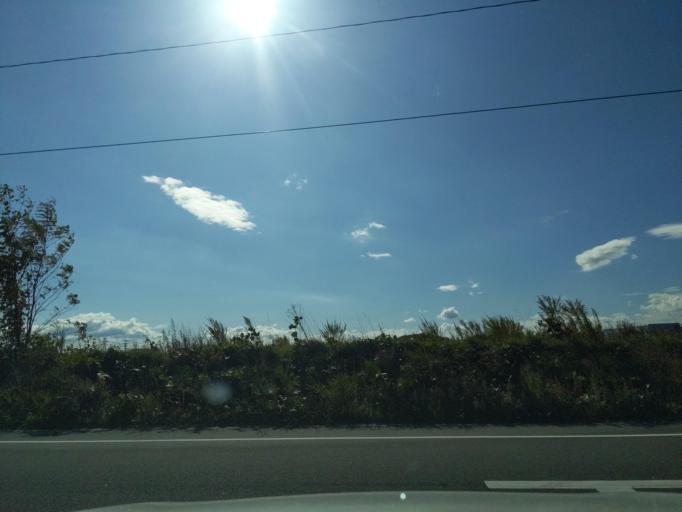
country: JP
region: Fukushima
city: Koriyama
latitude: 37.4641
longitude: 140.3000
